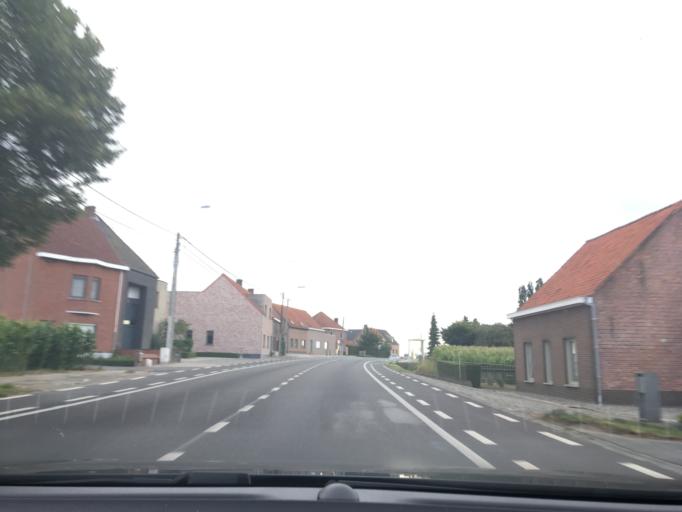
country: BE
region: Flanders
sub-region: Provincie West-Vlaanderen
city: Staden
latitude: 50.9262
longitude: 3.0069
